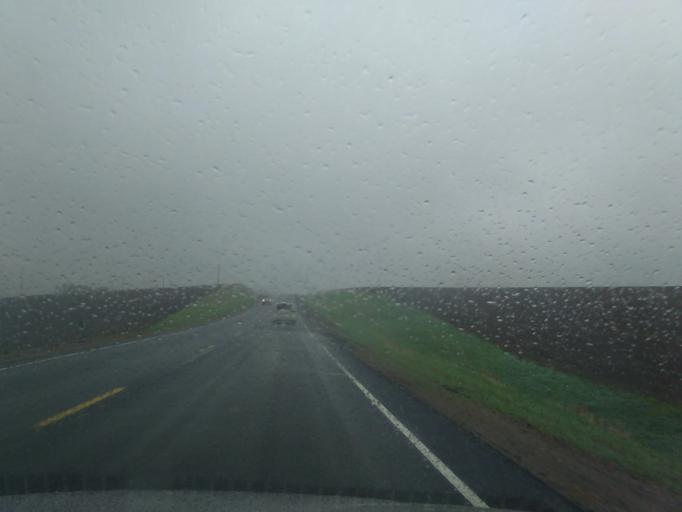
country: US
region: Nebraska
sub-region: Wayne County
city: Wayne
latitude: 42.1835
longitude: -97.1802
